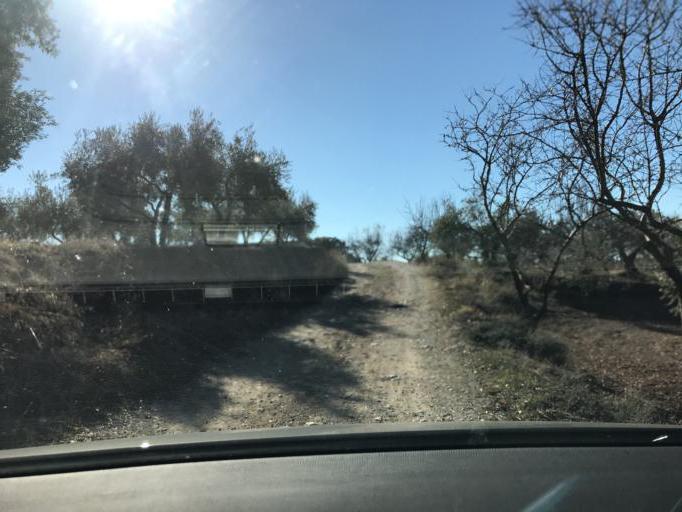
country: ES
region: Andalusia
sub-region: Provincia de Granada
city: Viznar
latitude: 37.2208
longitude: -3.5537
